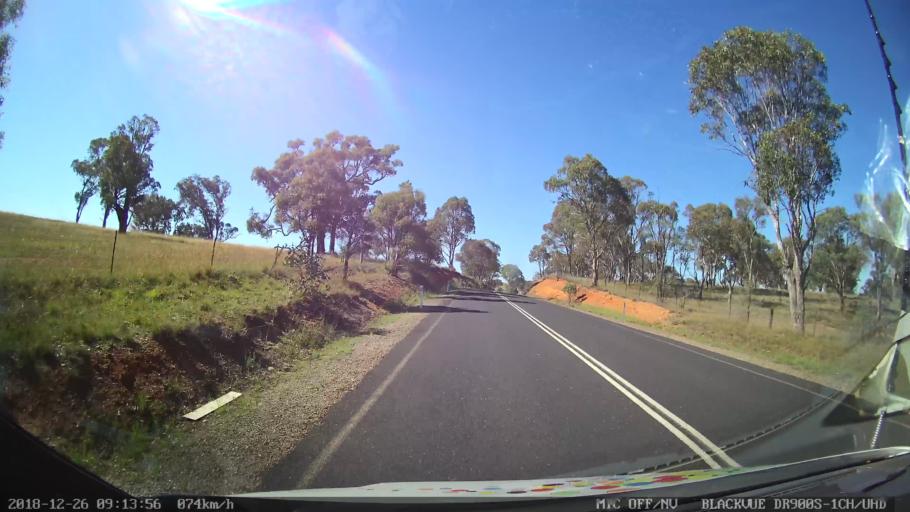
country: AU
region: New South Wales
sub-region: Mid-Western Regional
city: Kandos
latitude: -32.7730
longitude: 149.9799
